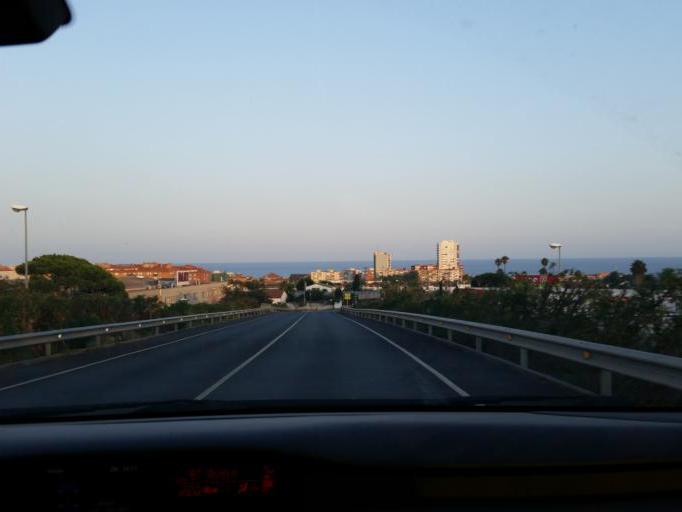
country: ES
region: Catalonia
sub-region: Provincia de Barcelona
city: Vilassar de Mar
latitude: 41.5126
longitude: 2.3807
